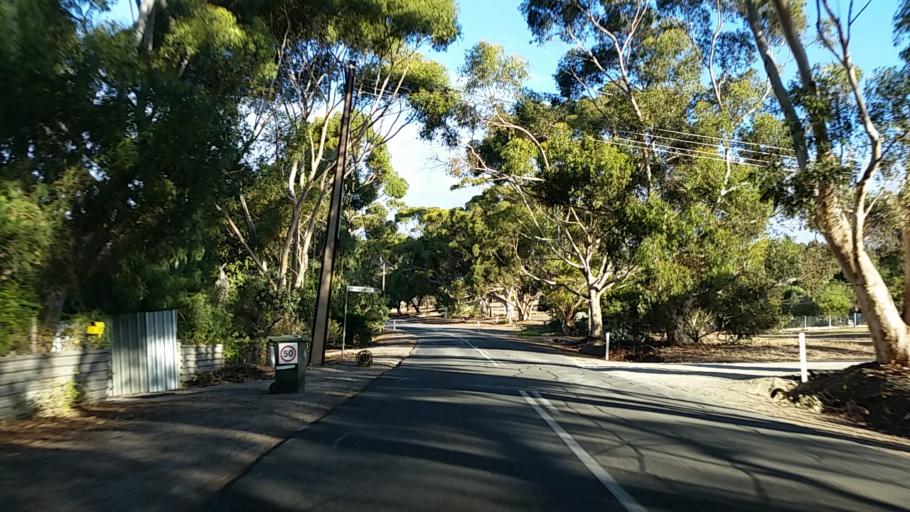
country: AU
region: South Australia
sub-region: Yankalilla
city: Normanville
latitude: -35.5245
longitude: 138.2249
